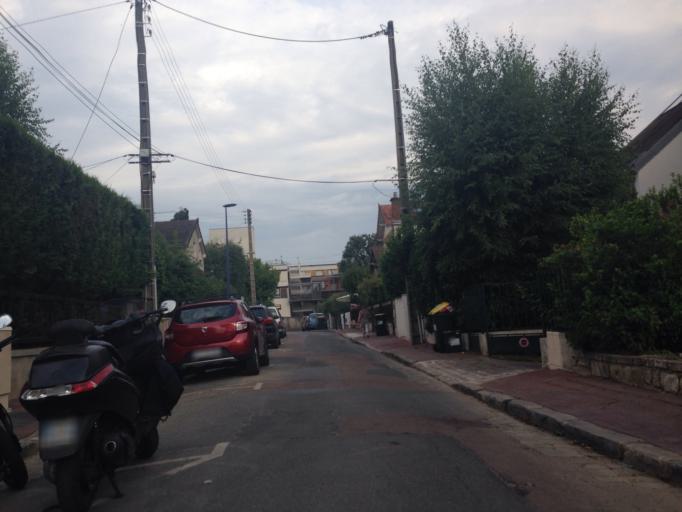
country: FR
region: Ile-de-France
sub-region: Departement des Hauts-de-Seine
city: Clamart
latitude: 48.8061
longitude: 2.2529
